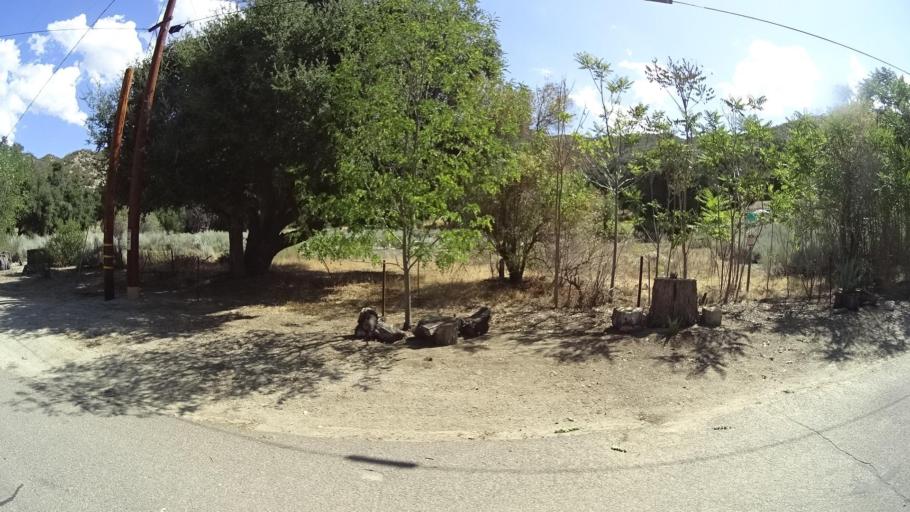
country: US
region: California
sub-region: San Diego County
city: Julian
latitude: 33.2865
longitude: -116.6151
